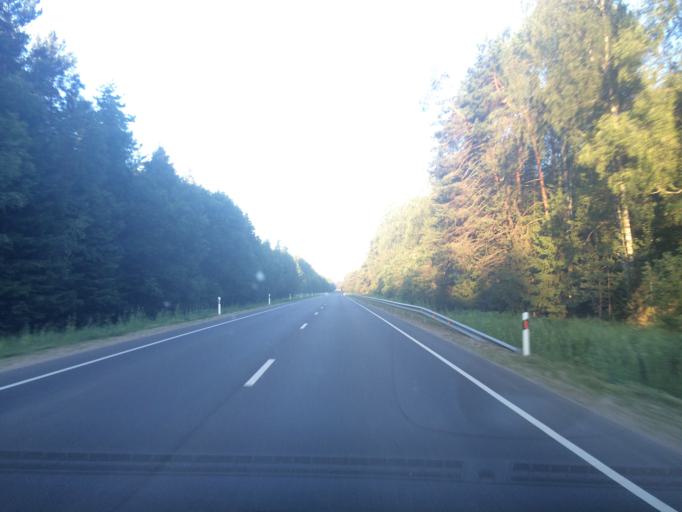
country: LT
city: Zarasai
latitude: 55.6859
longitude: 26.1291
